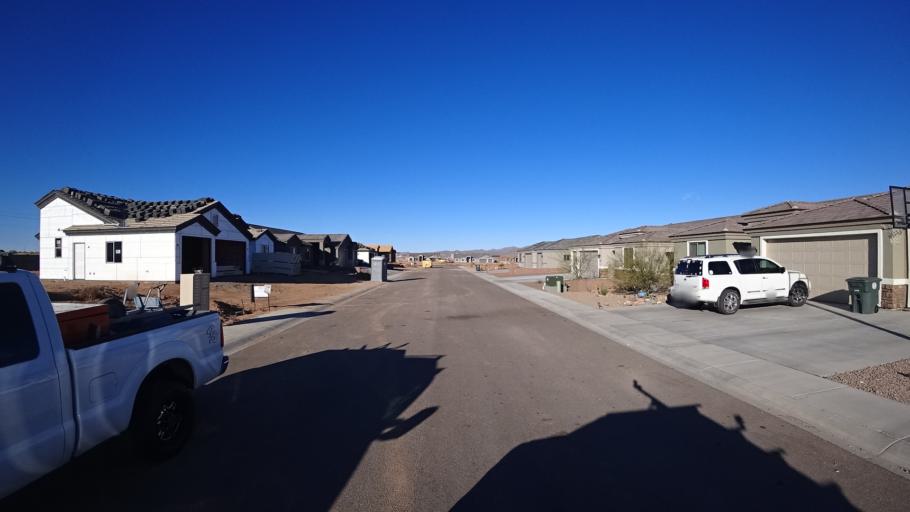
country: US
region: Arizona
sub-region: Mohave County
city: New Kingman-Butler
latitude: 35.2185
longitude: -113.9721
